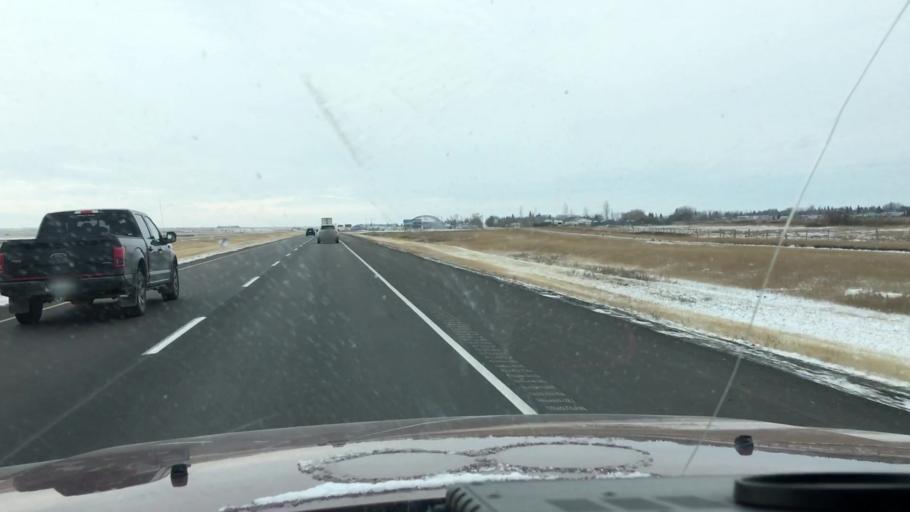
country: CA
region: Saskatchewan
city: Saskatoon
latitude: 51.8220
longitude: -106.4998
